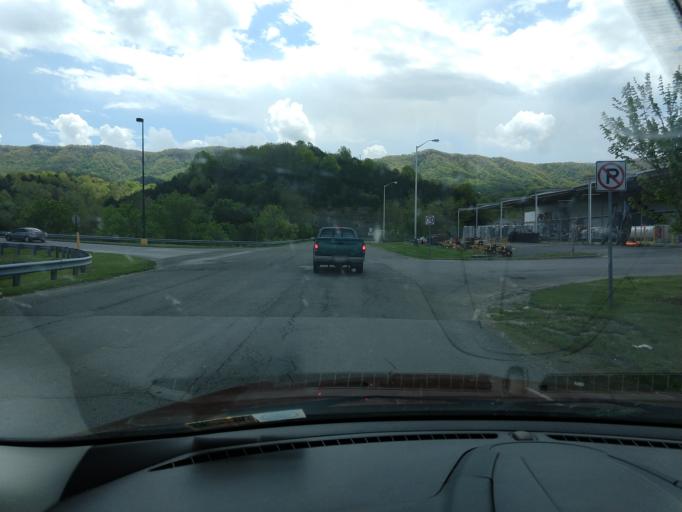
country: US
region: Virginia
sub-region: Tazewell County
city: Claypool Hill
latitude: 37.0658
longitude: -81.7342
